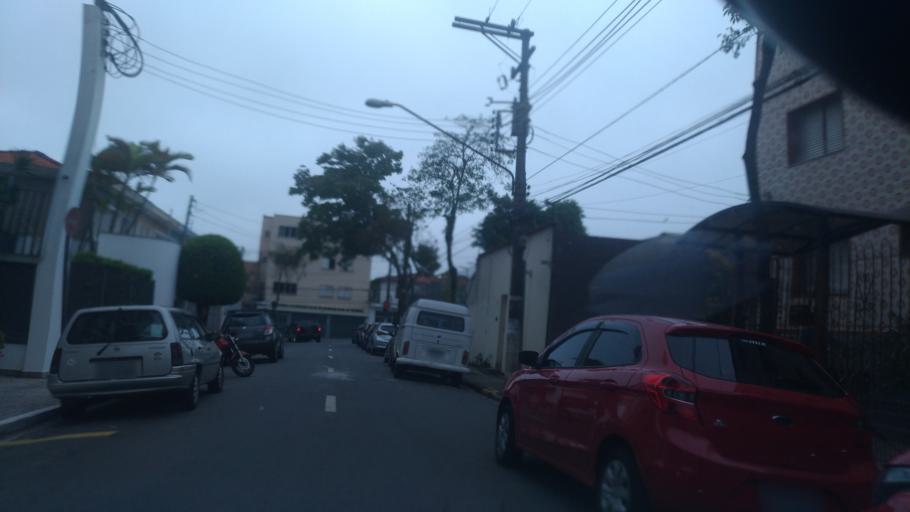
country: BR
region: Sao Paulo
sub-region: Sao Bernardo Do Campo
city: Sao Bernardo do Campo
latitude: -23.6975
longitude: -46.5587
